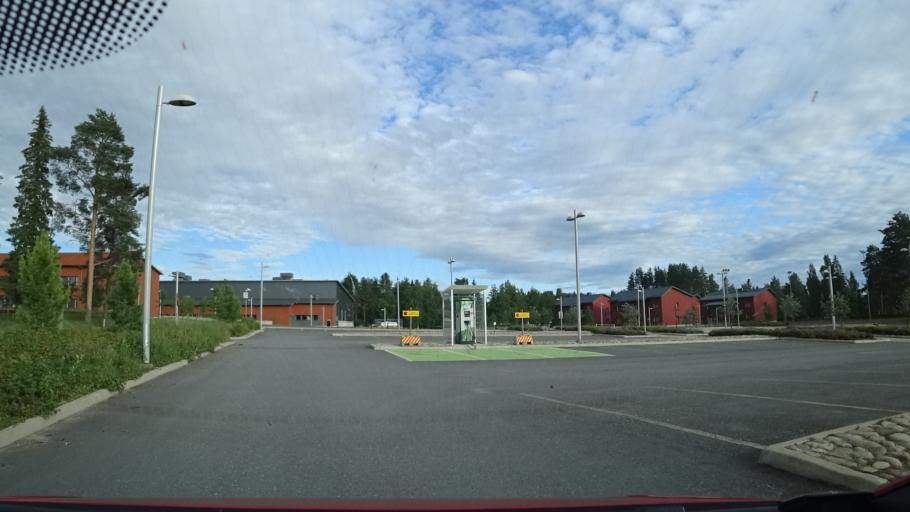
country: FI
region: Northern Ostrobothnia
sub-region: Oulu
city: Haukipudas
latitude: 65.1960
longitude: 25.4122
